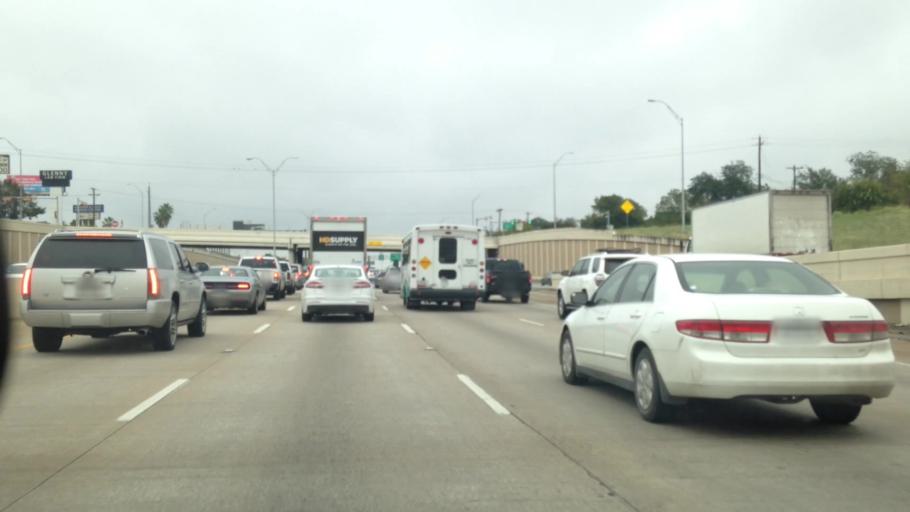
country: US
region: Texas
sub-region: Bexar County
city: Balcones Heights
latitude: 29.5061
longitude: -98.5452
